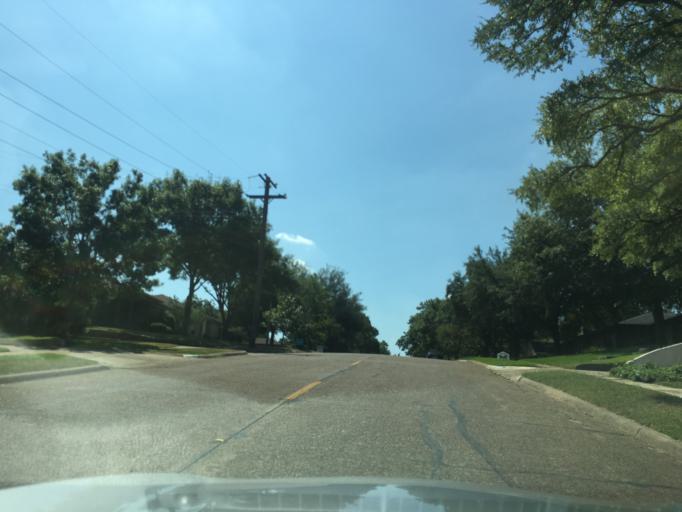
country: US
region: Texas
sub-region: Dallas County
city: Garland
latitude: 32.8544
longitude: -96.6926
